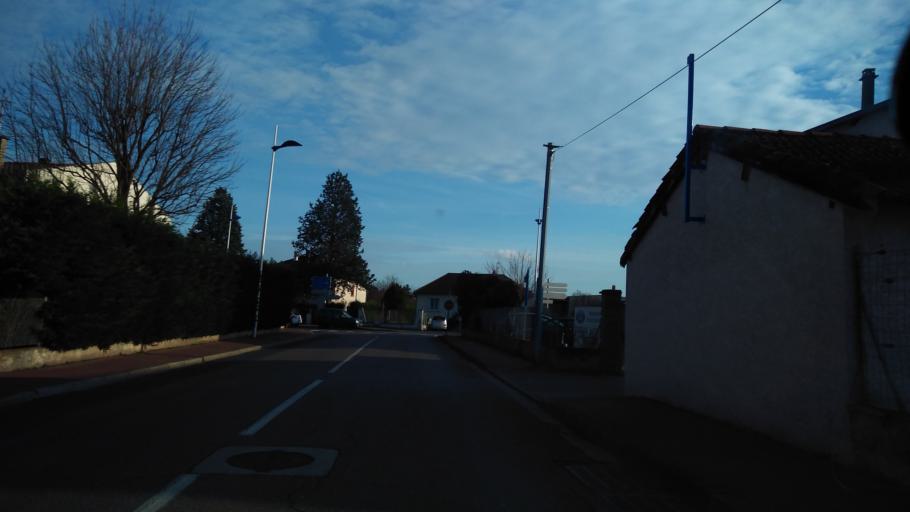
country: FR
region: Rhone-Alpes
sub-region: Departement du Rhone
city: Corbas
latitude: 45.6724
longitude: 4.9057
